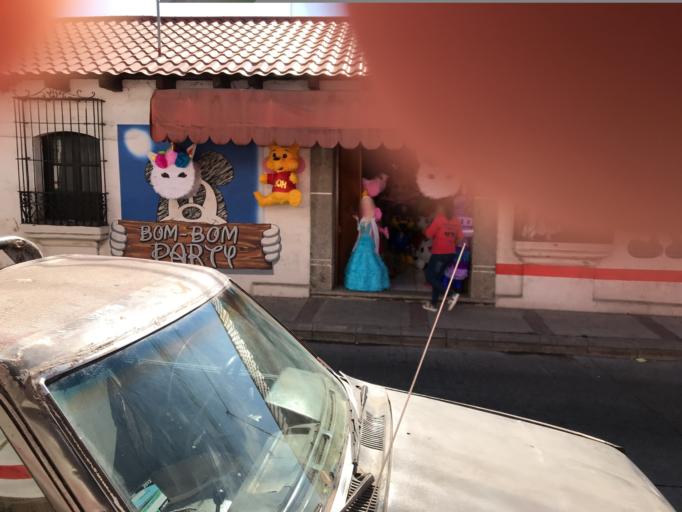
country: GT
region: Guatemala
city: Amatitlan
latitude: 14.4794
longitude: -90.6210
